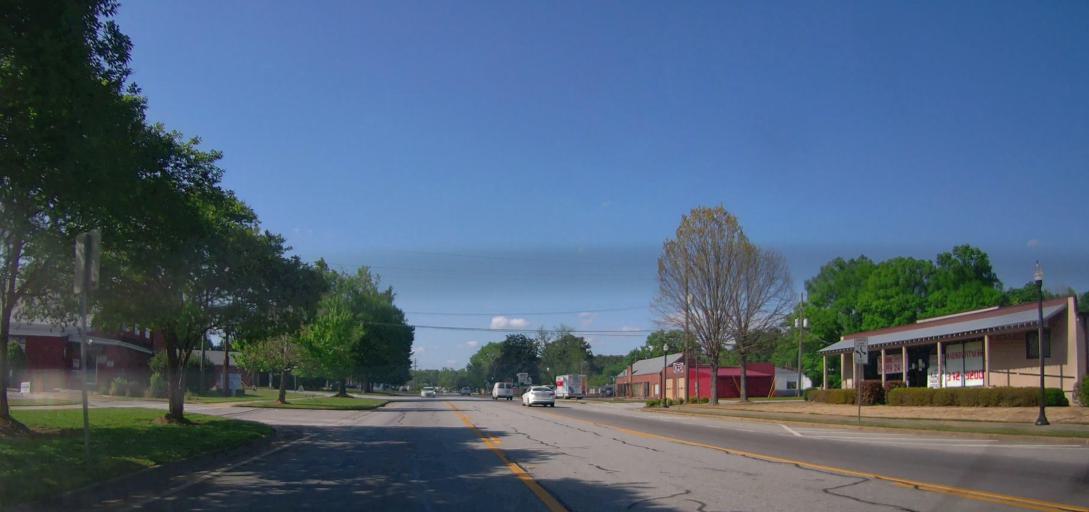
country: US
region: Georgia
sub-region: Morgan County
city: Madison
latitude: 33.5774
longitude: -83.4773
